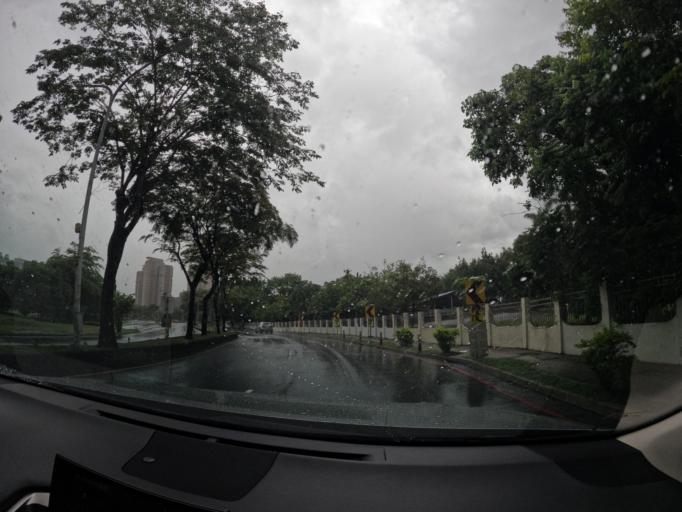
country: TW
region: Taiwan
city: Fengshan
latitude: 22.6553
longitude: 120.3568
